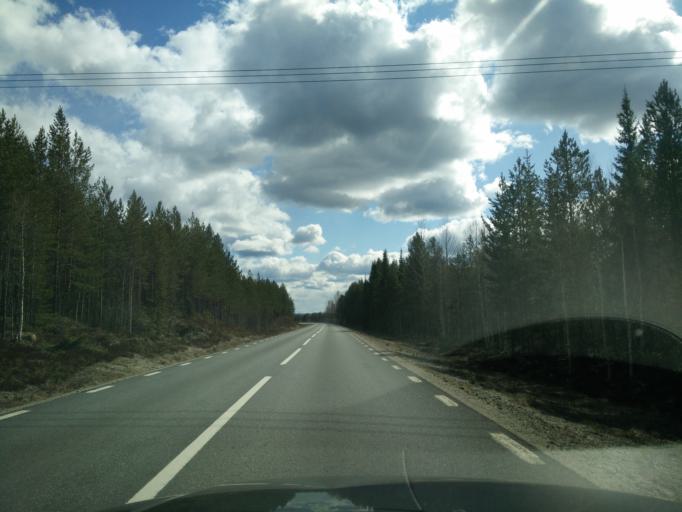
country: SE
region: Jaemtland
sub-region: Braecke Kommun
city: Braecke
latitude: 62.4567
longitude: 14.9683
